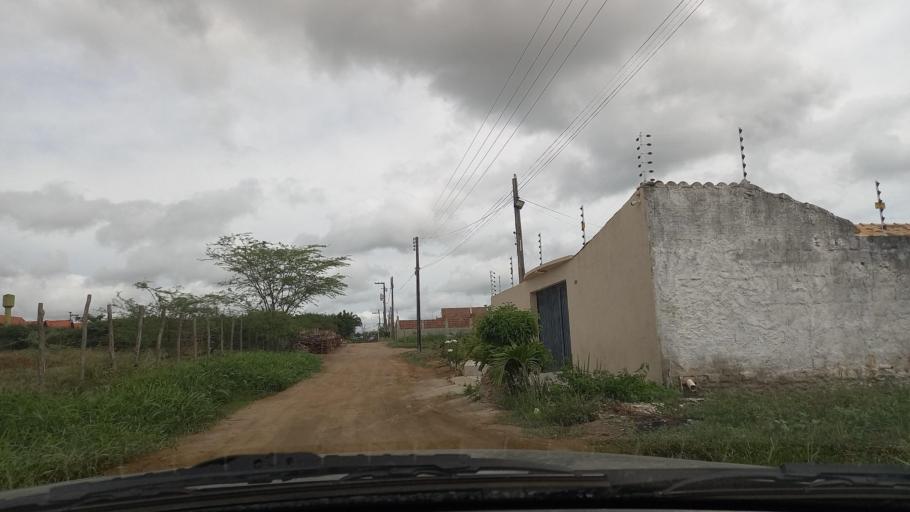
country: ET
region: Oromiya
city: Gore
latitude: 8.1899
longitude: 35.5822
